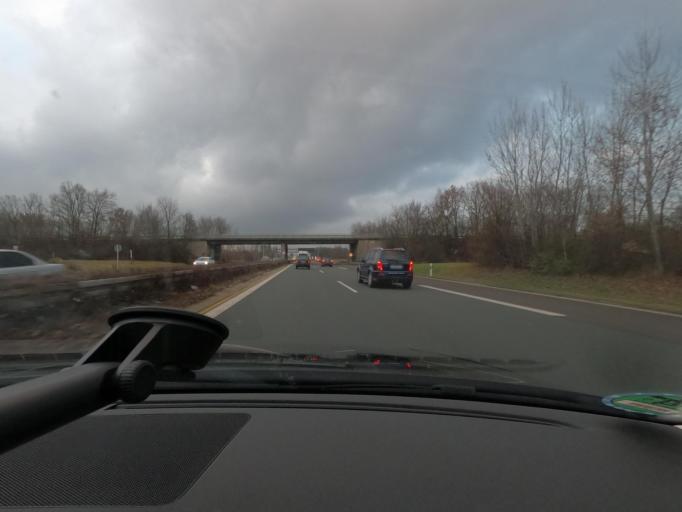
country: DE
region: Bavaria
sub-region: Regierungsbezirk Mittelfranken
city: Erlangen
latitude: 49.5402
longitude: 10.9929
